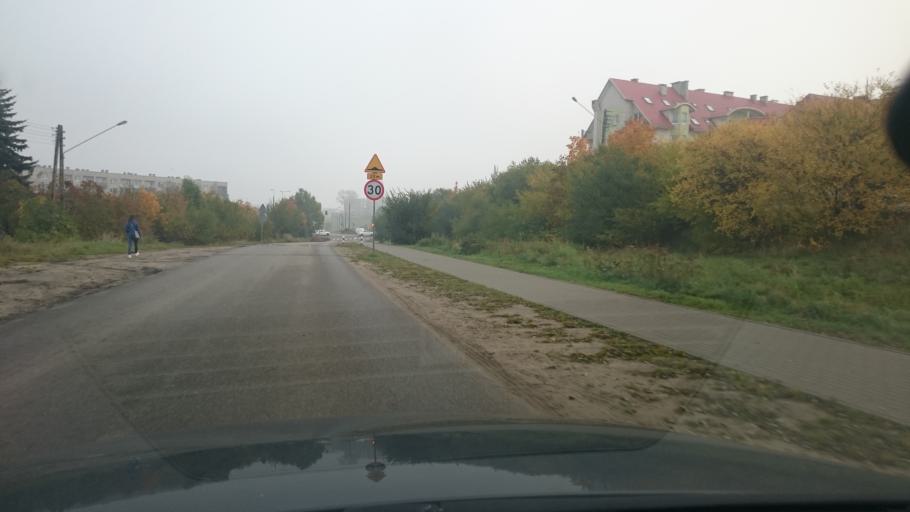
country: PL
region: Pomeranian Voivodeship
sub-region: Gdynia
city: Wielki Kack
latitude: 54.4682
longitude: 18.4989
